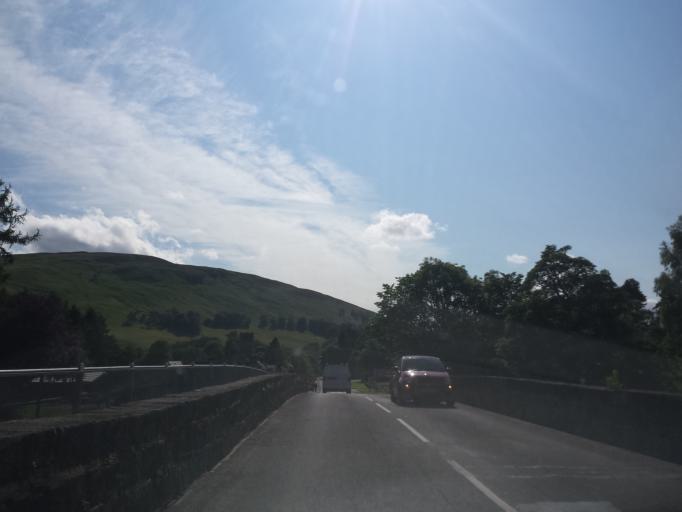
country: GB
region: Scotland
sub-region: Perth and Kinross
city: Pitlochry
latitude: 56.7677
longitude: -3.8406
